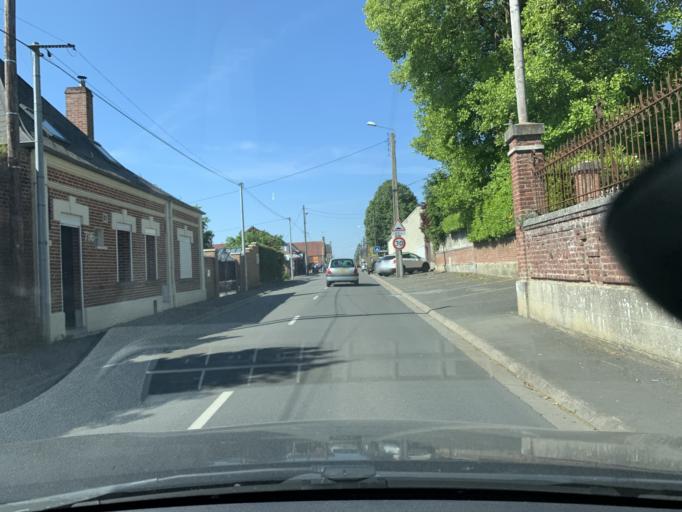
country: FR
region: Nord-Pas-de-Calais
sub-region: Departement du Nord
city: Masnieres
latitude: 50.0946
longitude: 3.2370
